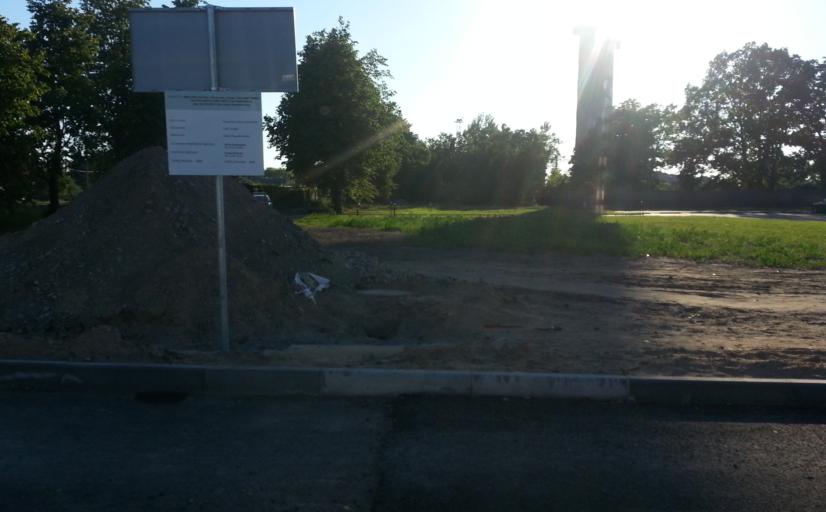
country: LT
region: Panevezys
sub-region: Panevezys City
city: Panevezys
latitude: 55.7442
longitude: 24.3703
